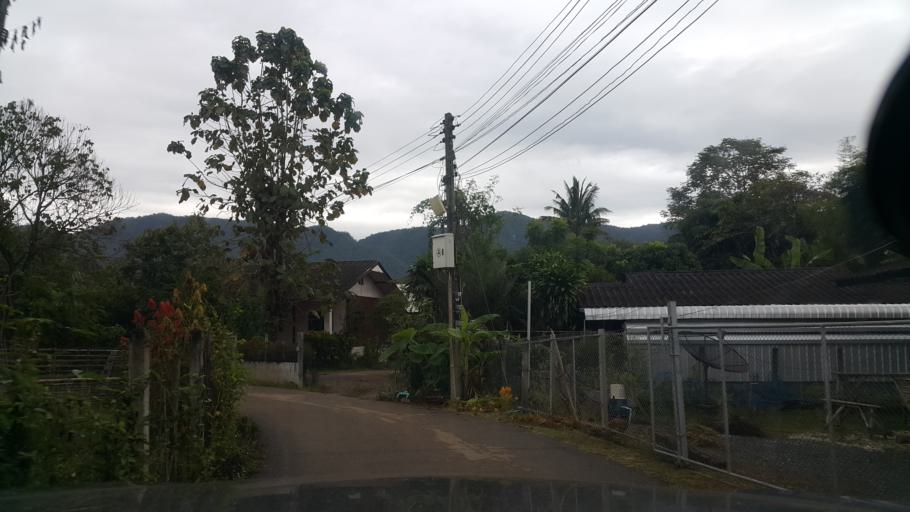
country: TH
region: Chiang Mai
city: Mae On
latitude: 18.7721
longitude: 99.2587
